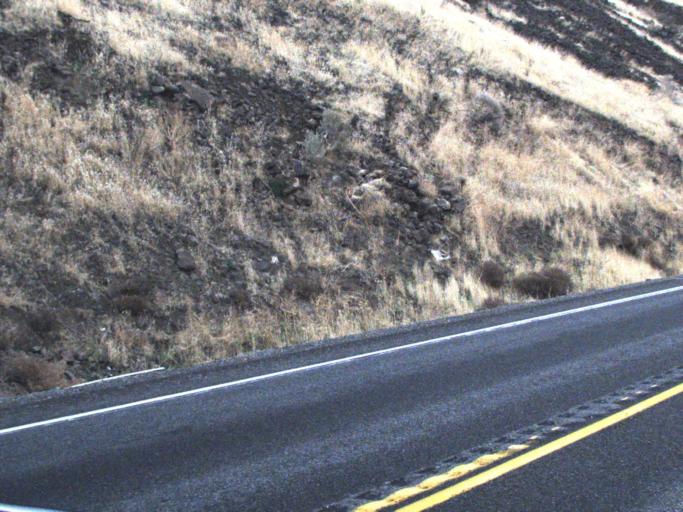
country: US
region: Washington
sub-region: Benton County
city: Finley
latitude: 46.0293
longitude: -118.9322
